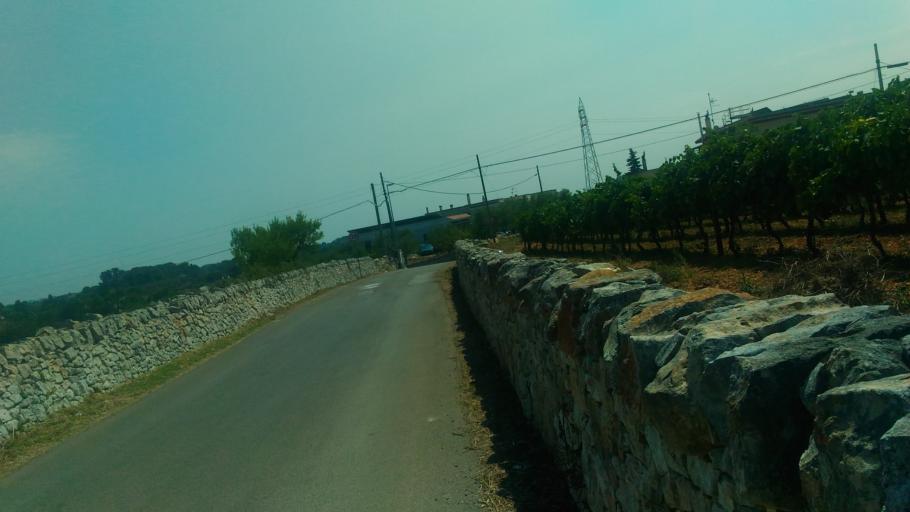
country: IT
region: Apulia
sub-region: Provincia di Brindisi
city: Cisternino
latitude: 40.7446
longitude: 17.3795
